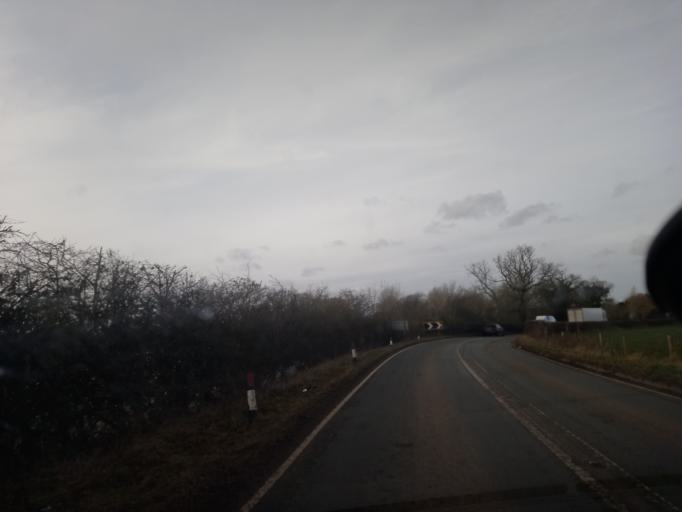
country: GB
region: England
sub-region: Shropshire
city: Prees
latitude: 52.8693
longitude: -2.6077
